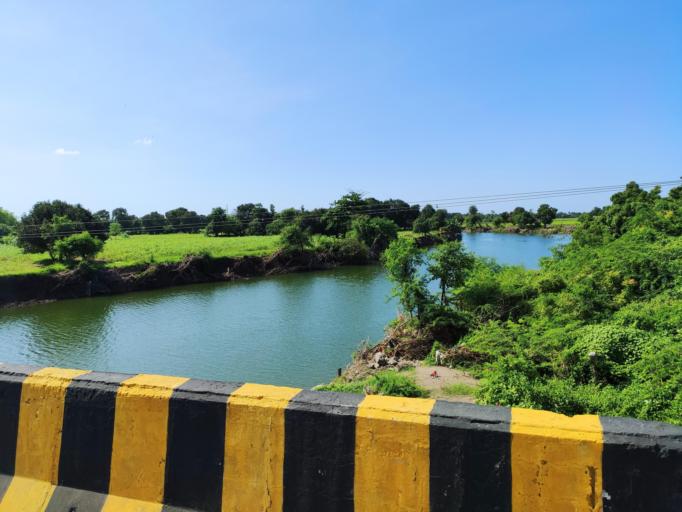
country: IN
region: Gujarat
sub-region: Jamnagar
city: Jamnagar
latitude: 22.4839
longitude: 70.1507
